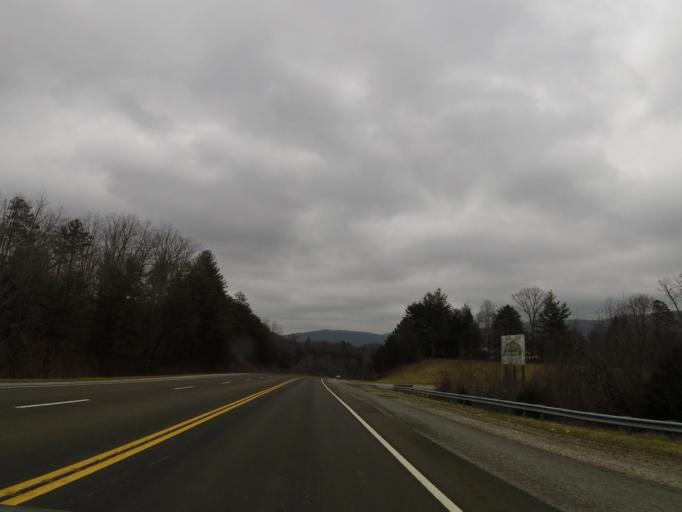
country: US
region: Tennessee
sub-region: Scott County
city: Huntsville
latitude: 36.3795
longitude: -84.3827
